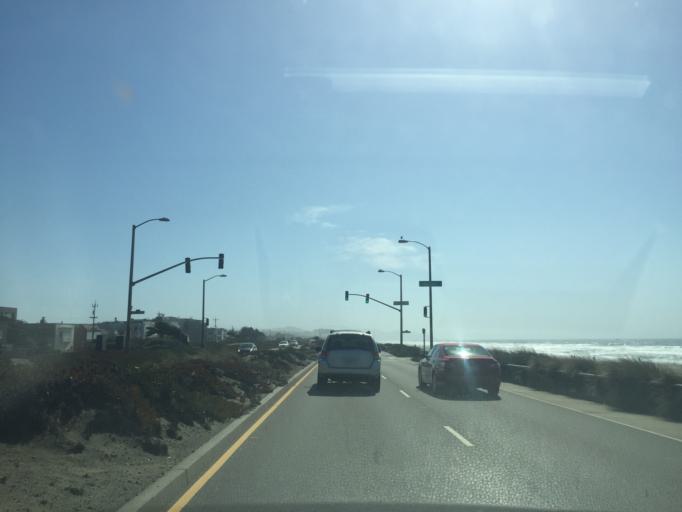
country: US
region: California
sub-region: San Mateo County
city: Daly City
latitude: 37.7497
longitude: -122.5085
